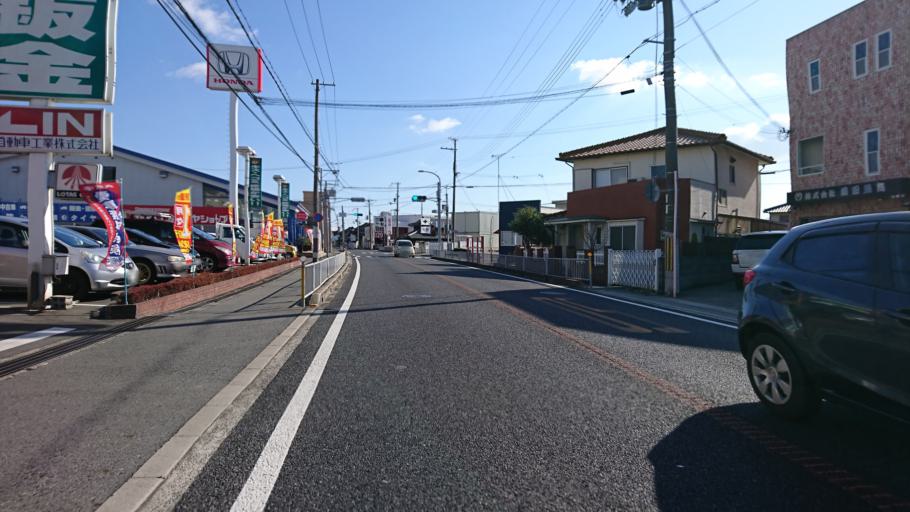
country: JP
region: Hyogo
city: Kakogawacho-honmachi
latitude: 34.7777
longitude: 134.8214
